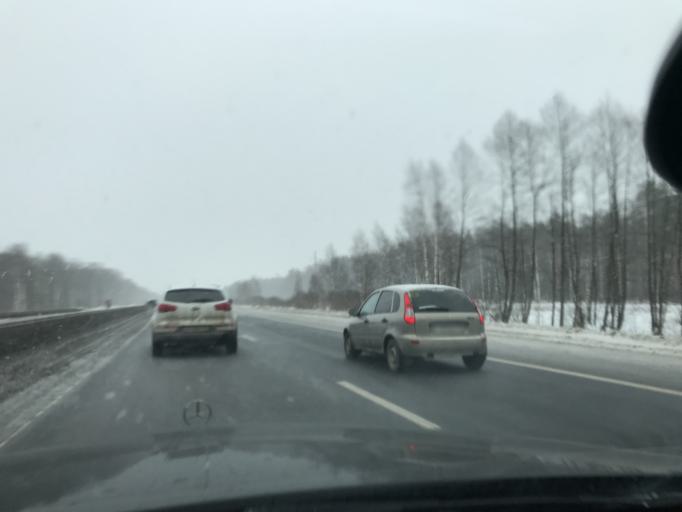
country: RU
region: Nizjnij Novgorod
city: Yuganets
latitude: 56.2903
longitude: 43.2831
